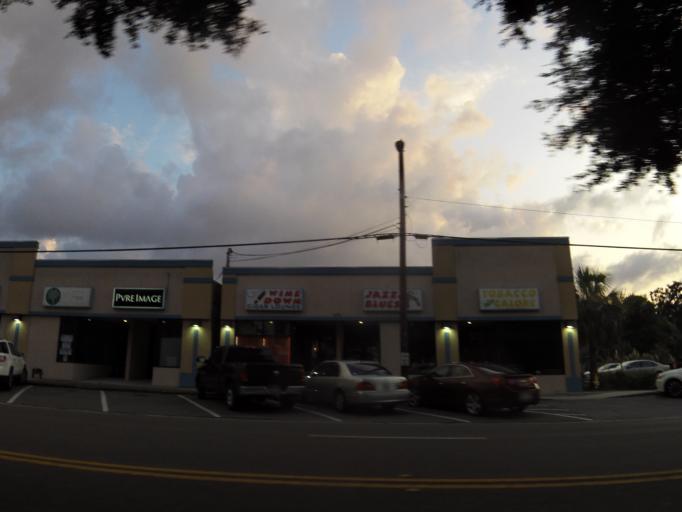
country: US
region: Florida
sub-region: Duval County
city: Jacksonville
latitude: 30.3108
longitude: -81.7166
